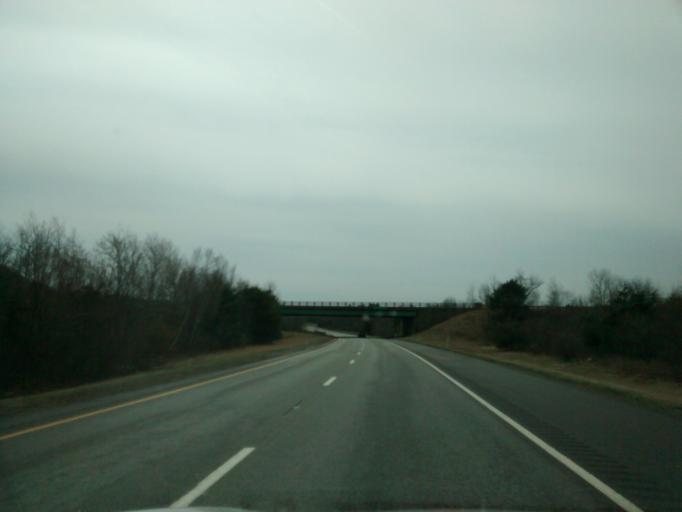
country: US
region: Massachusetts
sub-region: Worcester County
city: Oxford
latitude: 42.1526
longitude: -71.8565
